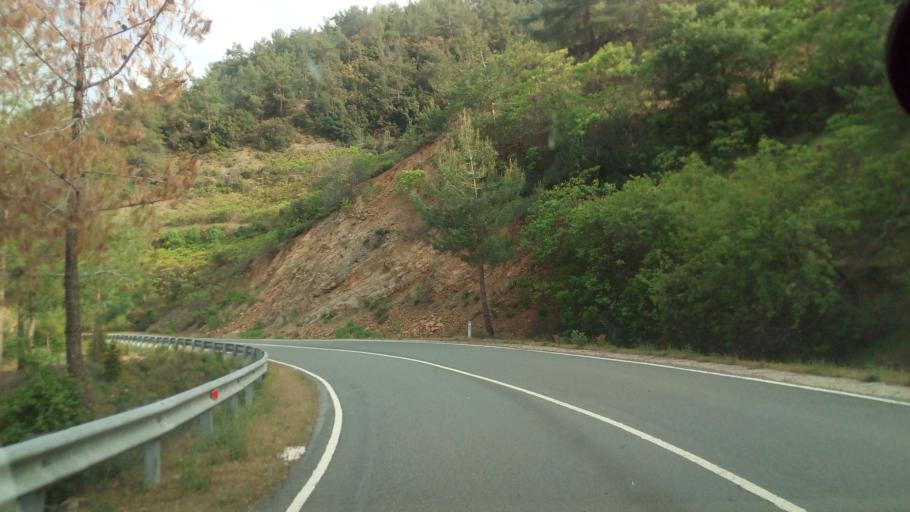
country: CY
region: Lefkosia
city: Kakopetria
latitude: 35.0008
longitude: 32.7936
